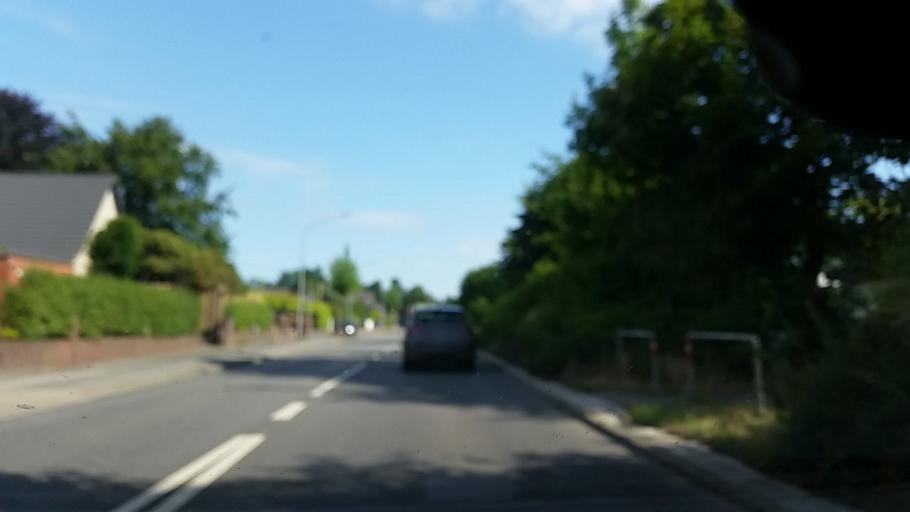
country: DE
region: Hamburg
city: Langenhorn
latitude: 53.6912
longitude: 10.0290
